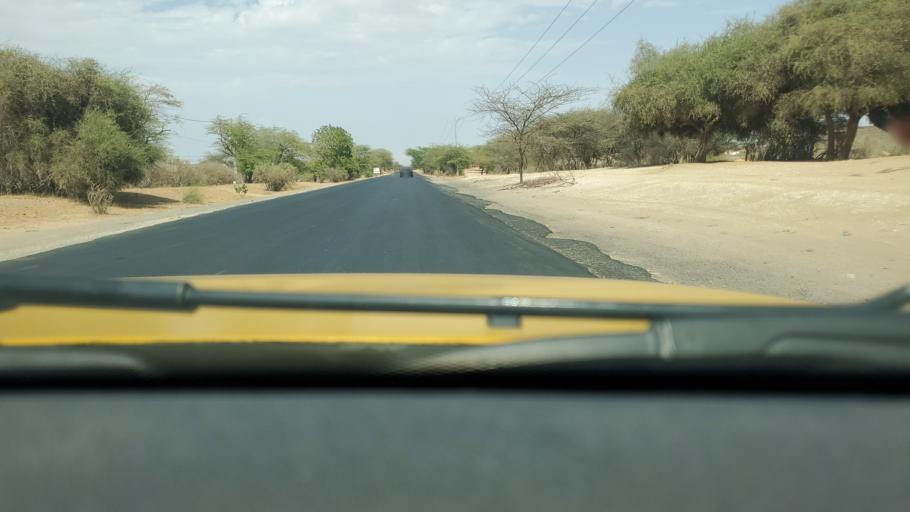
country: SN
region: Saint-Louis
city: Saint-Louis
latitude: 15.9228
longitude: -16.3909
